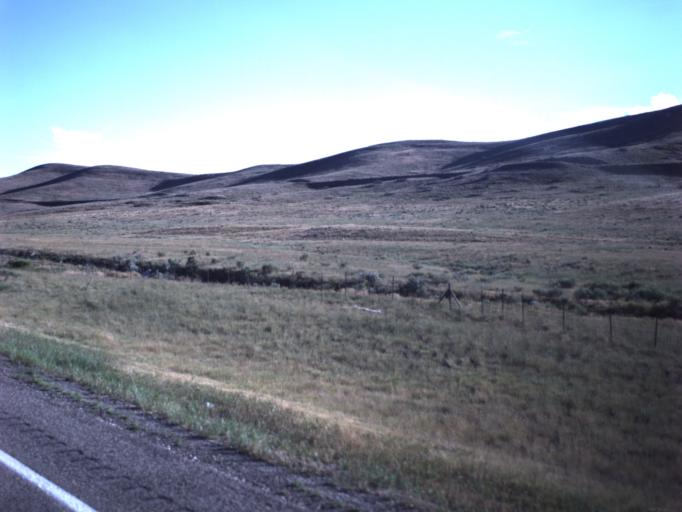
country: US
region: Utah
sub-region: Sanpete County
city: Fairview
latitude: 39.7448
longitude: -111.4774
